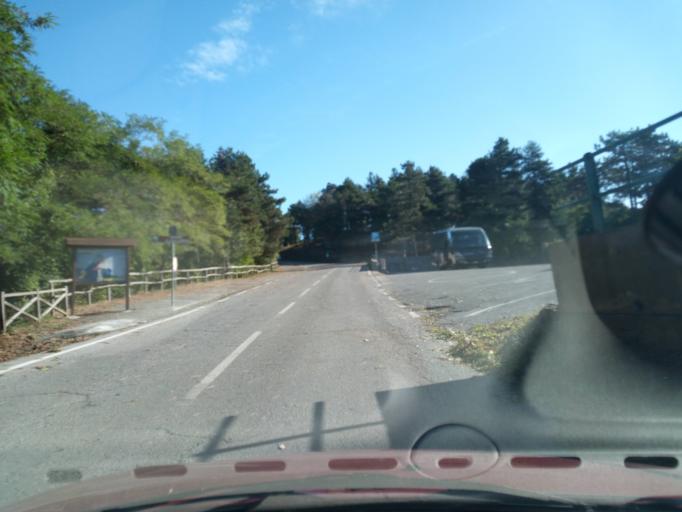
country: IT
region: Liguria
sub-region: Provincia di Genova
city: Campomorone
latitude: 44.4872
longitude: 8.8608
